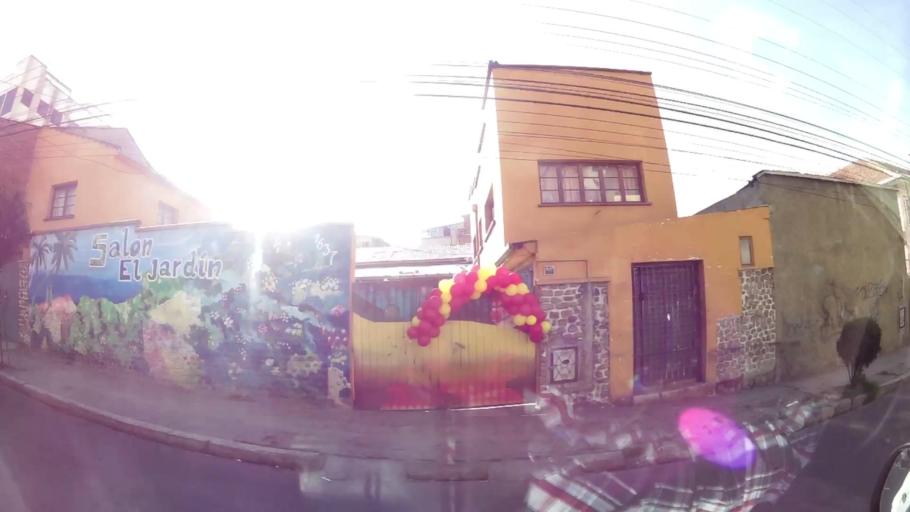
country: BO
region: La Paz
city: La Paz
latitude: -16.4984
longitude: -68.1202
